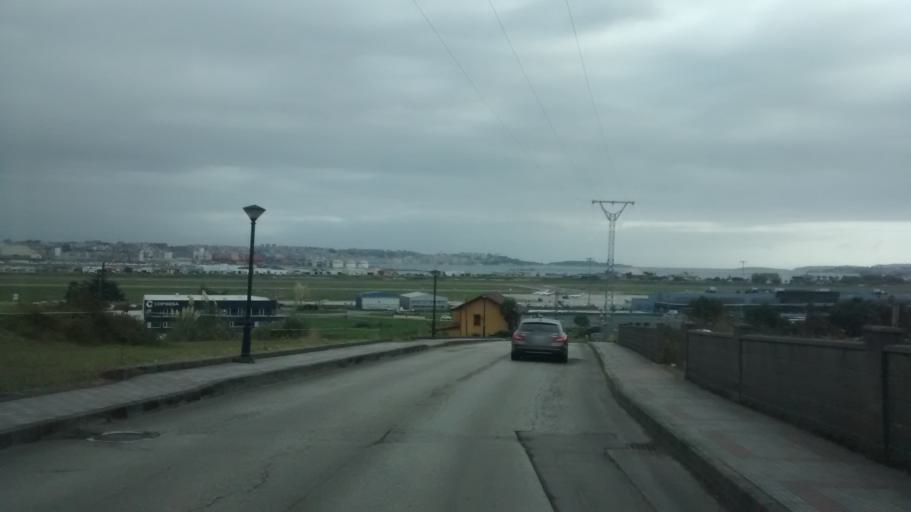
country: ES
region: Cantabria
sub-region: Provincia de Cantabria
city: El Astillero
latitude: 43.4205
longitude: -3.8300
